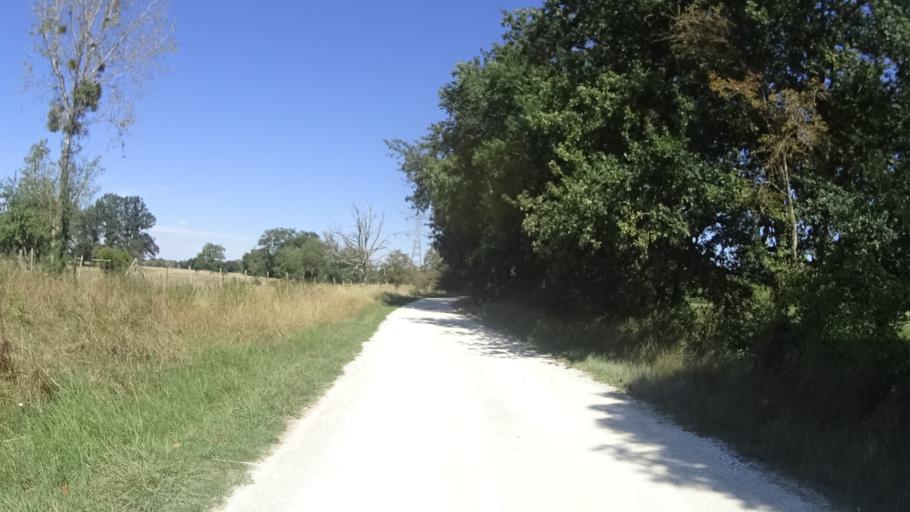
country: FR
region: Bourgogne
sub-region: Departement de la Nievre
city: Neuvy-sur-Loire
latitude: 47.5228
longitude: 2.8617
